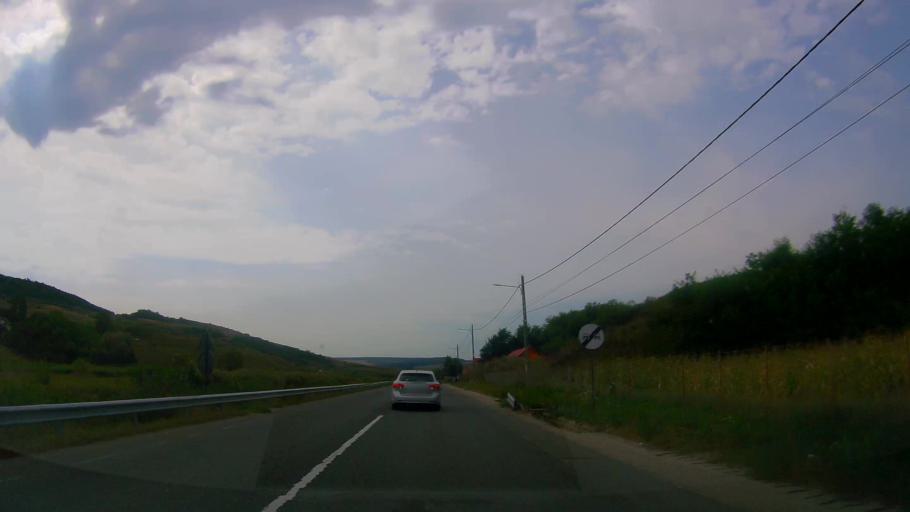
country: RO
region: Cluj
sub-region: Comuna Sanpaul
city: Sanpaul
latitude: 46.8675
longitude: 23.4123
